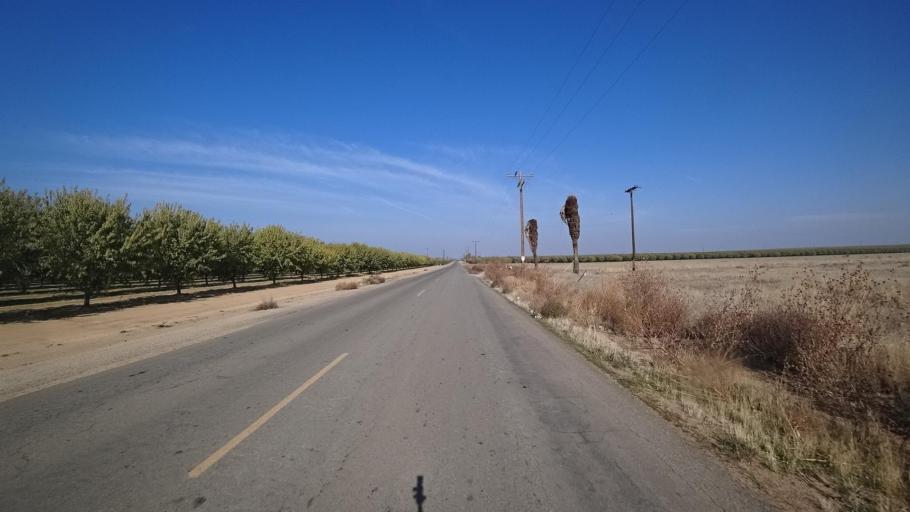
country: US
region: California
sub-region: Kern County
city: McFarland
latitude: 35.6633
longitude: -119.1690
